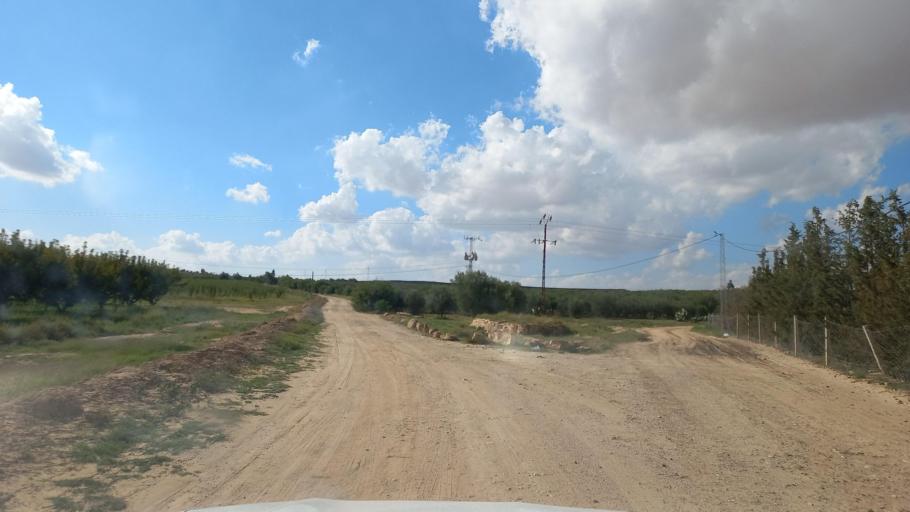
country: TN
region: Al Qasrayn
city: Sbiba
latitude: 35.3352
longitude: 9.0868
